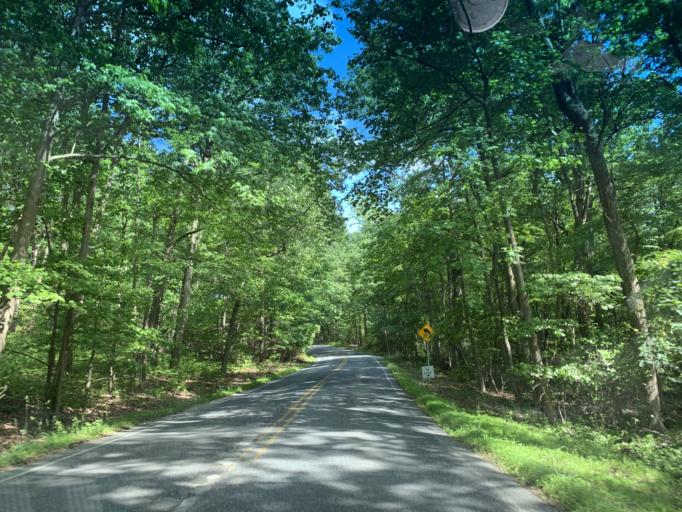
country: US
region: Maryland
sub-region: Cecil County
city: Charlestown
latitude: 39.5468
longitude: -75.9440
